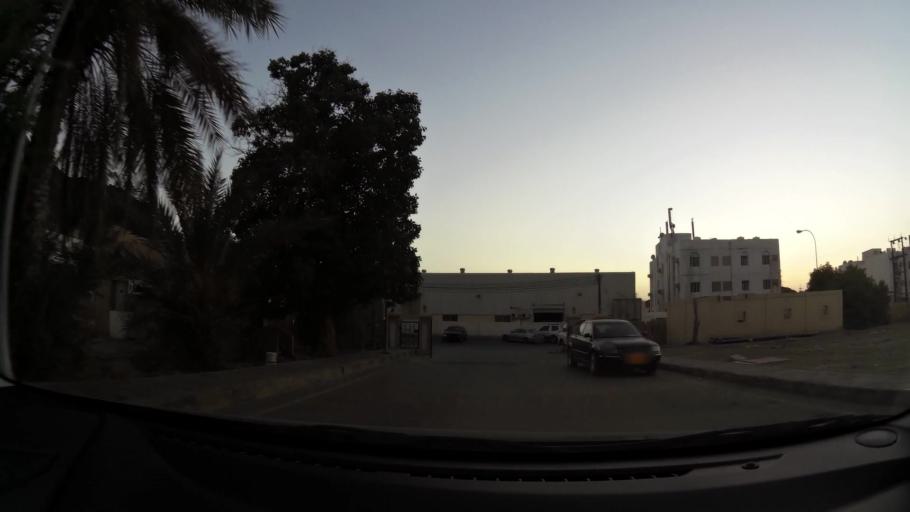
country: OM
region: Muhafazat Masqat
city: Muscat
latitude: 23.5920
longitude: 58.5670
